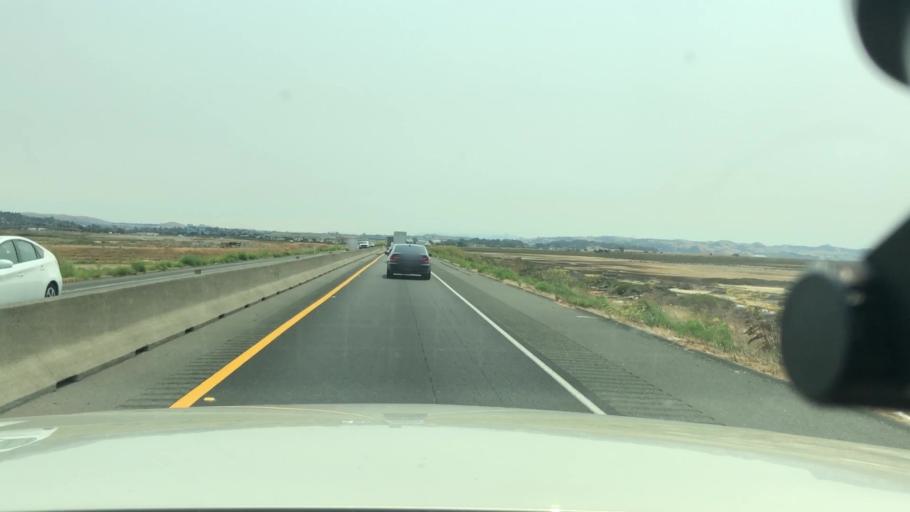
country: US
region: California
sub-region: Solano County
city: Vallejo
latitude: 38.1207
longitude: -122.3105
